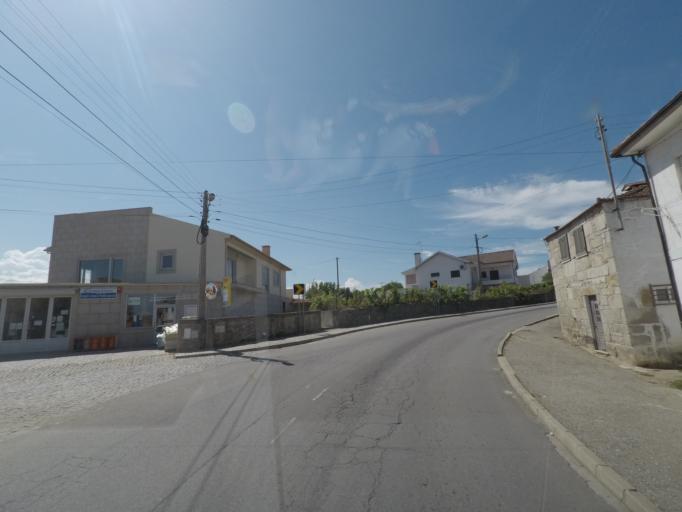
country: PT
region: Vila Real
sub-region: Sabrosa
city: Sabrosa
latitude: 41.2644
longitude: -7.4800
